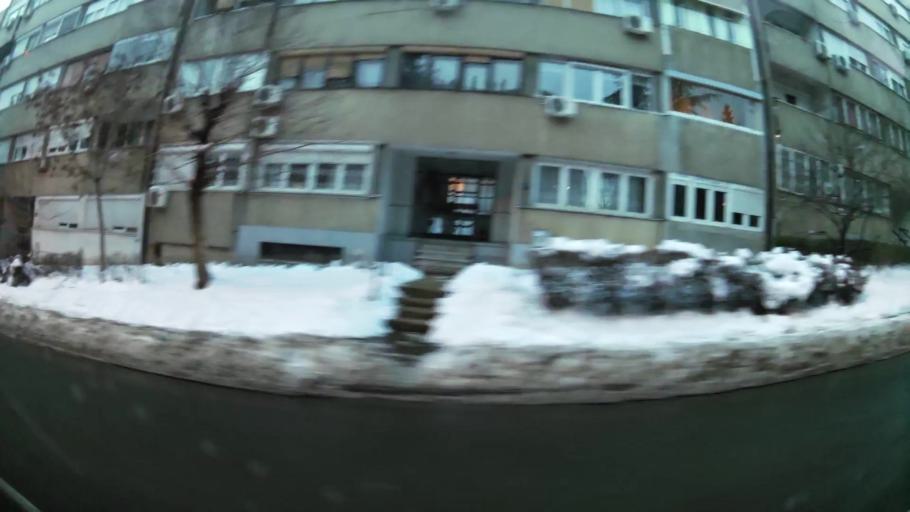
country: RS
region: Central Serbia
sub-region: Belgrade
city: Palilula
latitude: 44.7989
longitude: 20.5053
